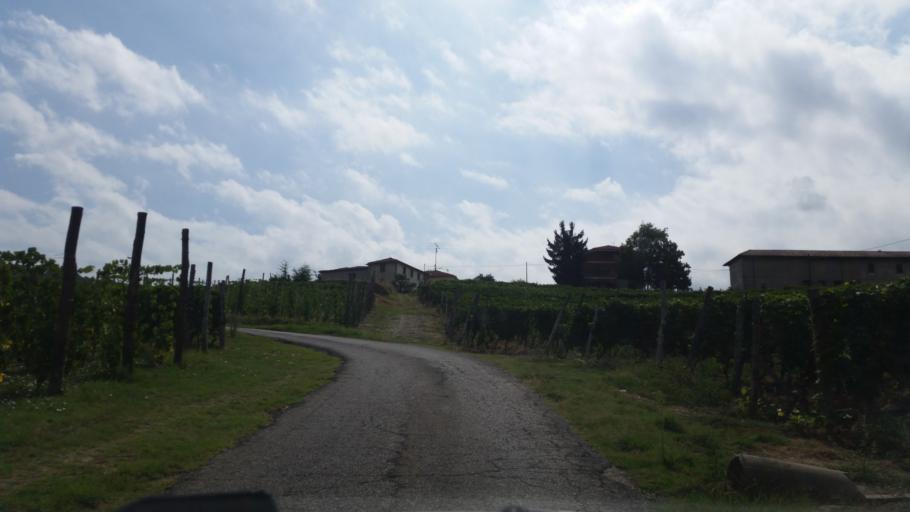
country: IT
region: Piedmont
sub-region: Provincia di Cuneo
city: Cossano Belbo
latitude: 44.6697
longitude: 8.2027
